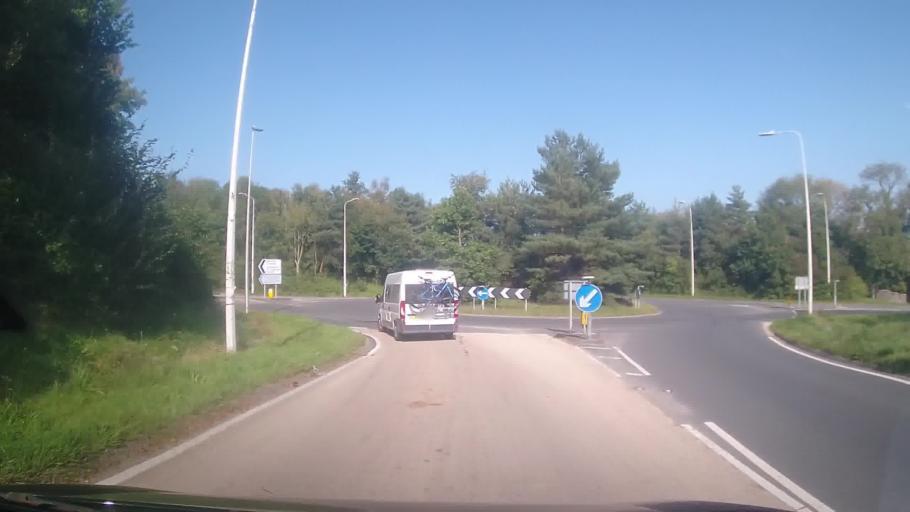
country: GB
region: Wales
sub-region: County of Ceredigion
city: Cardigan
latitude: 52.0759
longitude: -4.6566
